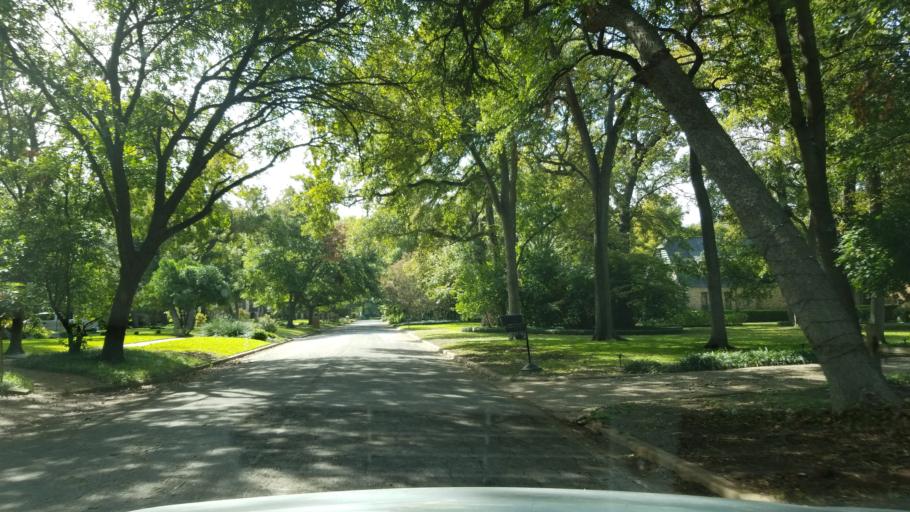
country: US
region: Texas
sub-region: Dallas County
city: Highland Park
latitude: 32.8101
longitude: -96.7176
